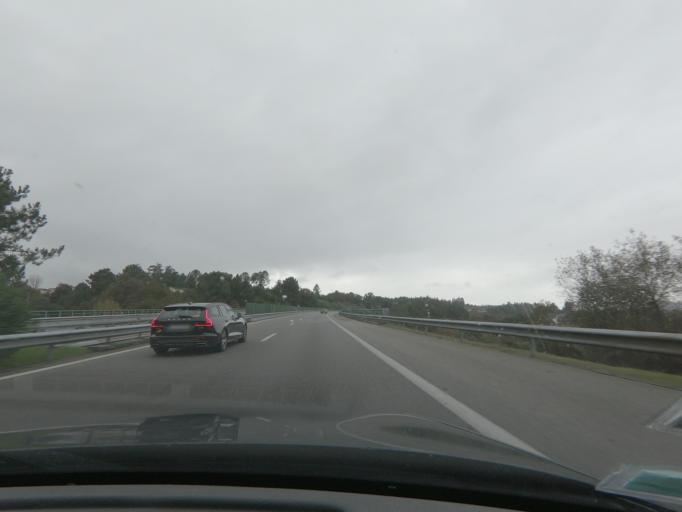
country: PT
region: Porto
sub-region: Marco de Canaveses
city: Marco de Canavezes
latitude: 41.2262
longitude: -8.1722
